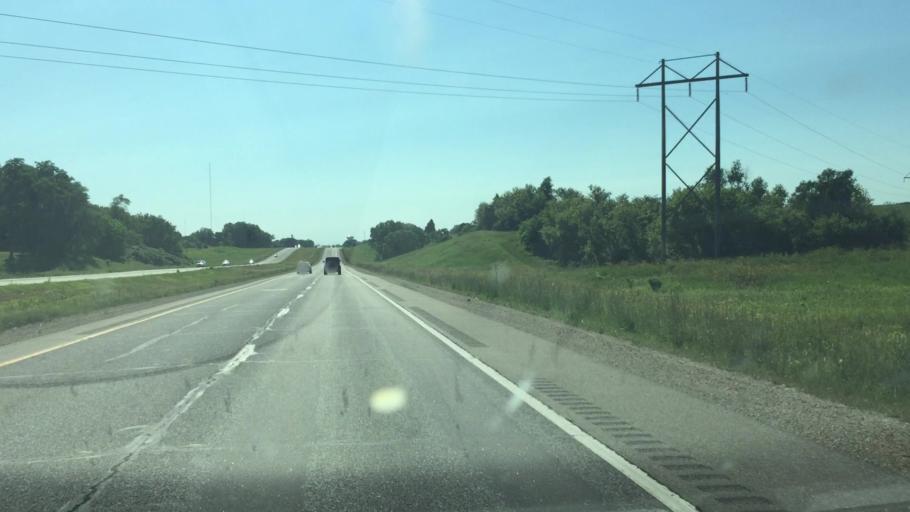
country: US
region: Iowa
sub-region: Linn County
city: Ely
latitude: 41.9260
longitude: -91.5943
